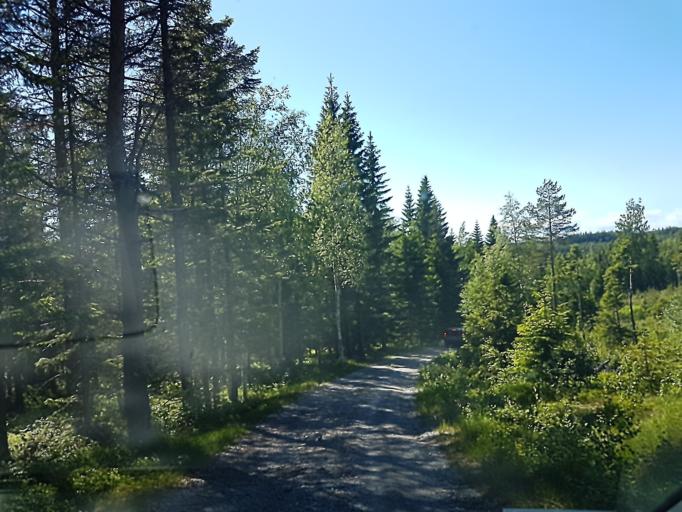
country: SE
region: Vaesternorrland
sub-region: OErnskoeldsviks Kommun
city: Bjasta
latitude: 63.1137
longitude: 18.4098
